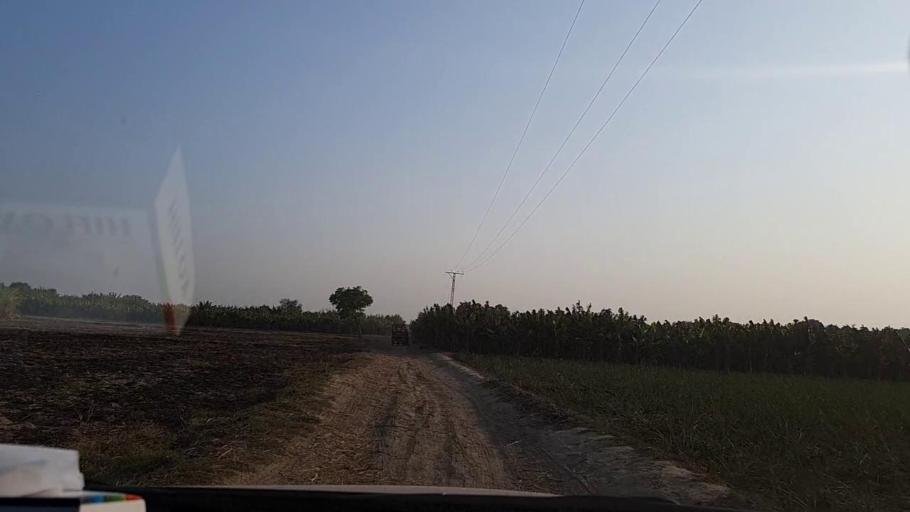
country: PK
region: Sindh
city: Tando Ghulam Ali
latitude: 25.2085
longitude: 68.9206
